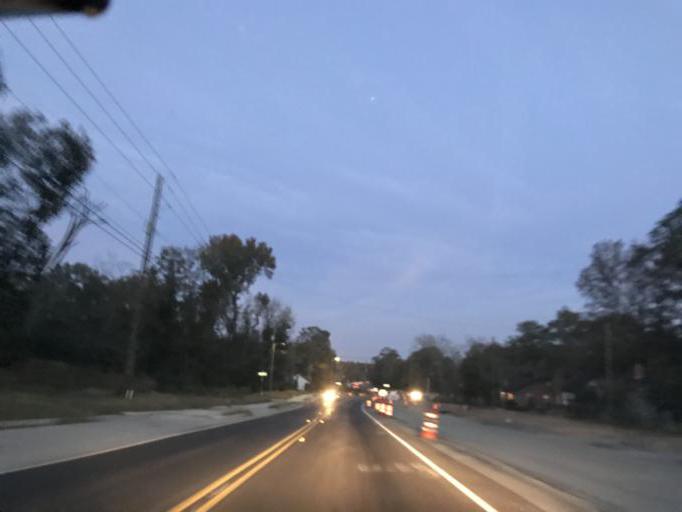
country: US
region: Georgia
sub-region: Bibb County
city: Macon
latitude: 32.8494
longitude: -83.6019
